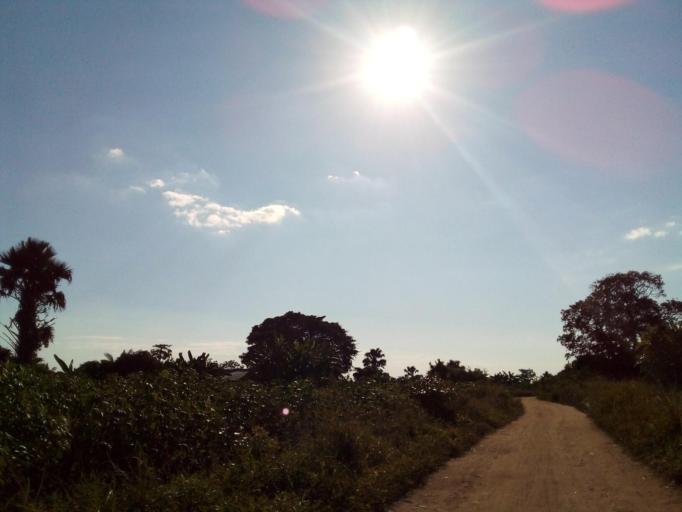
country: MZ
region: Zambezia
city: Quelimane
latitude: -17.5270
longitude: 36.6819
